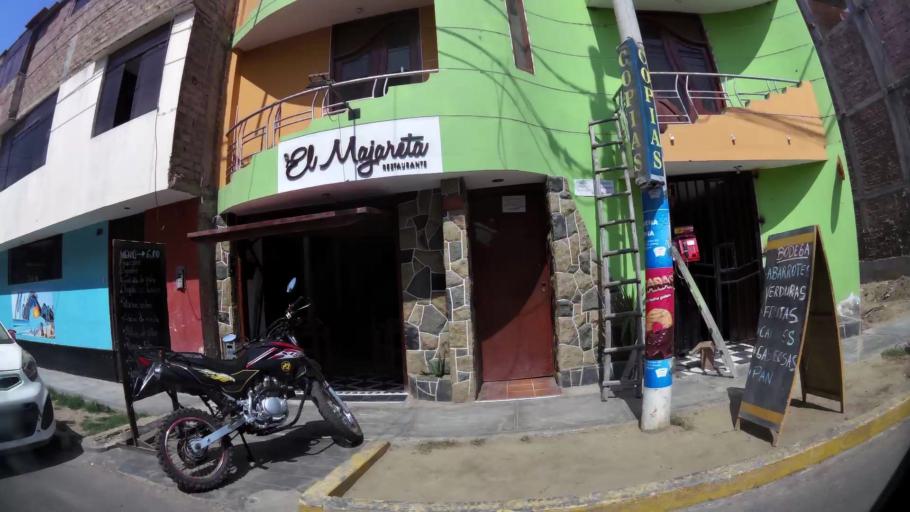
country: PE
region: La Libertad
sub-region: Provincia de Trujillo
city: Buenos Aires
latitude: -8.1256
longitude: -79.0436
